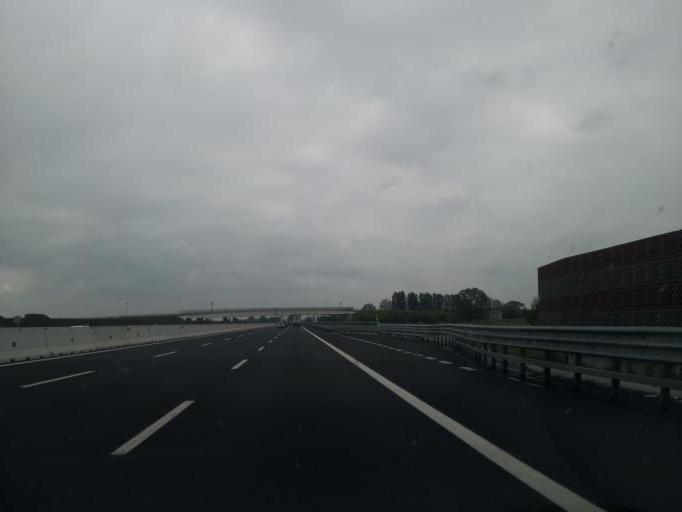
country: IT
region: Veneto
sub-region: Provincia di Venezia
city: Meolo
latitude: 45.6445
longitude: 12.4712
